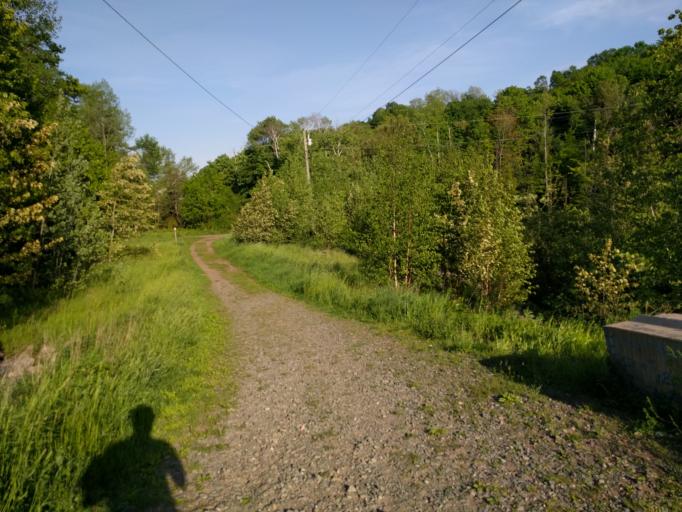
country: US
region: Michigan
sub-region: Marquette County
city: Trowbridge Park
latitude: 46.5656
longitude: -87.4451
